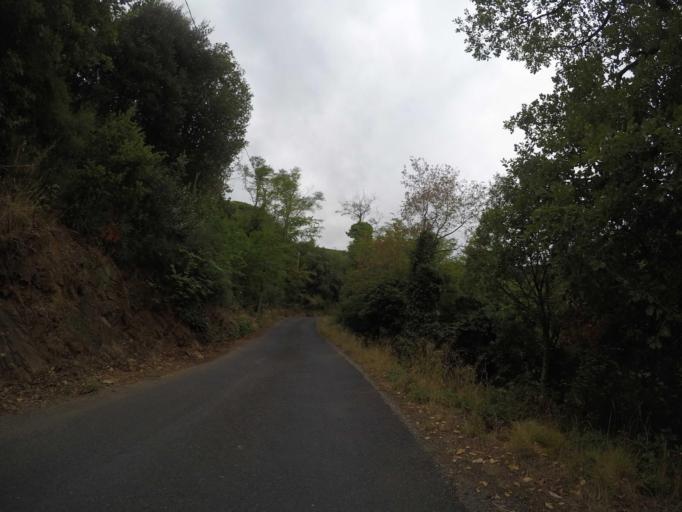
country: FR
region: Languedoc-Roussillon
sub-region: Departement des Pyrenees-Orientales
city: Ille-sur-Tet
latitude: 42.6352
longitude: 2.6208
